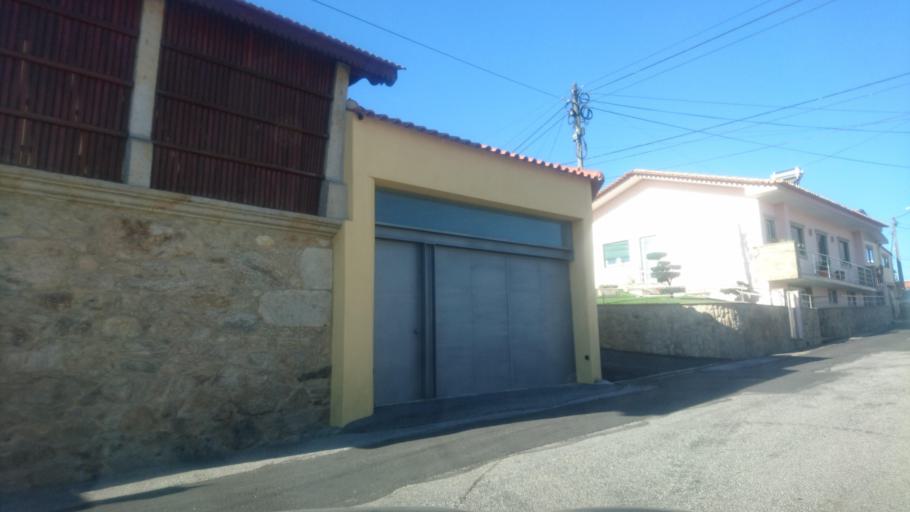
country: PT
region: Aveiro
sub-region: Oliveira de Azemeis
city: Sao Roque
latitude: 40.8725
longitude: -8.4656
